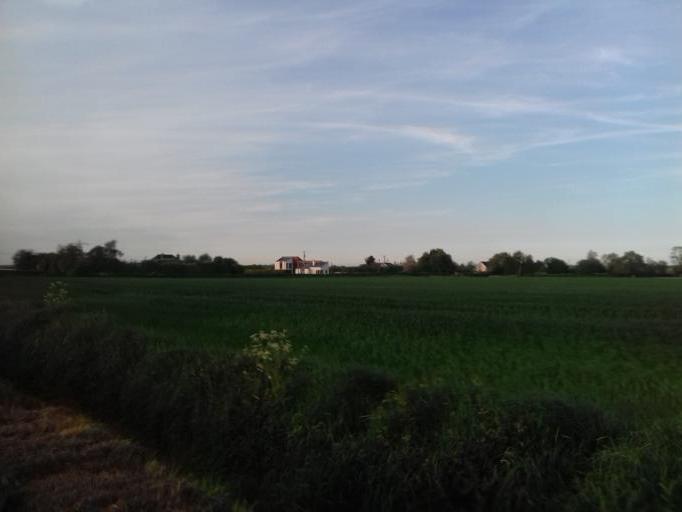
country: IE
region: Leinster
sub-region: Fingal County
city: Swords
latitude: 53.4844
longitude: -6.2258
